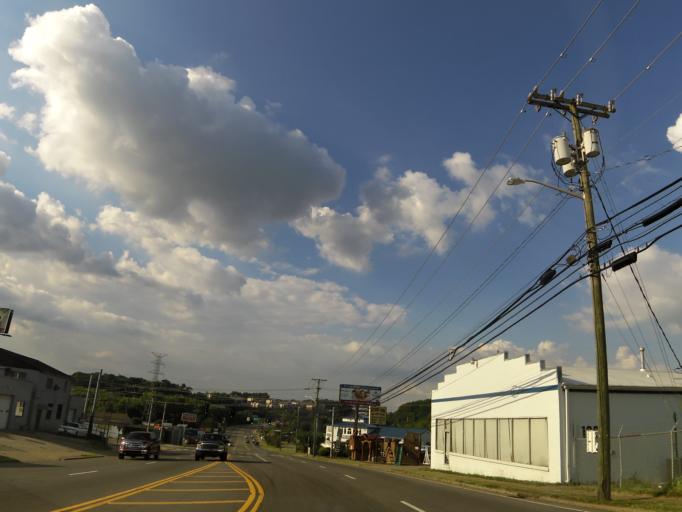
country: US
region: Tennessee
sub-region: Montgomery County
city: Clarksville
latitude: 36.5379
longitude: -87.3378
